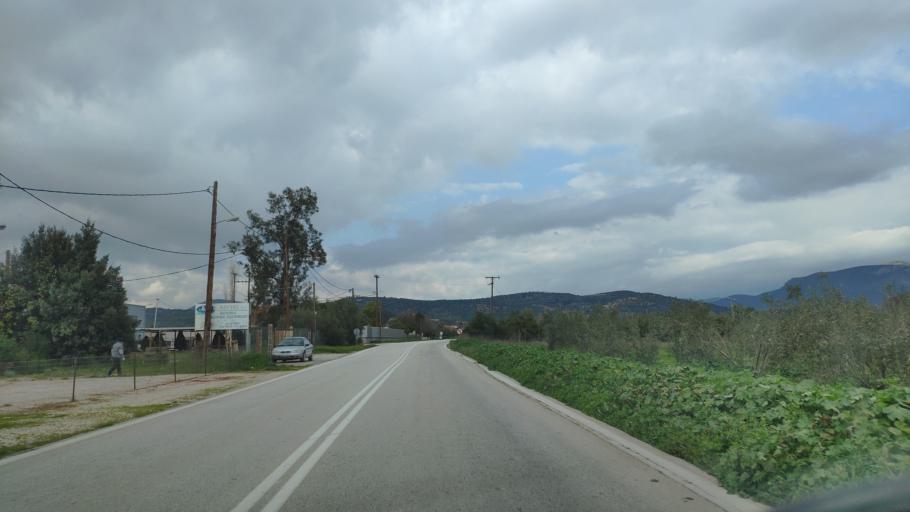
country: GR
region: Peloponnese
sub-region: Nomos Argolidos
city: Koutsopodi
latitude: 37.7137
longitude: 22.7254
